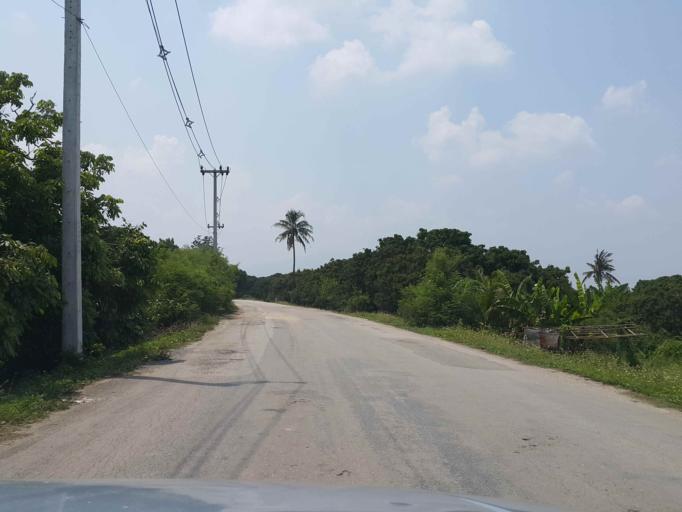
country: TH
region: Chiang Mai
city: Saraphi
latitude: 18.6745
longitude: 99.0095
